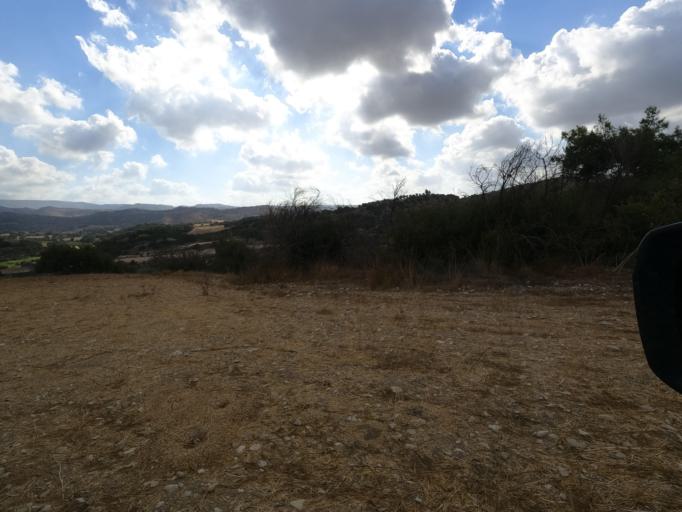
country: CY
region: Pafos
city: Mesogi
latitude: 34.8421
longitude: 32.5414
